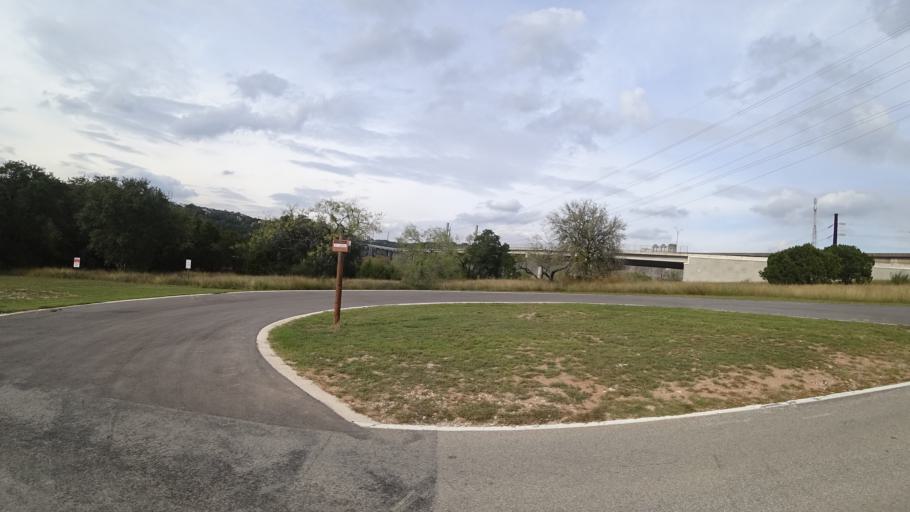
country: US
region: Texas
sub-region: Travis County
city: Hudson Bend
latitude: 30.3871
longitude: -97.9082
